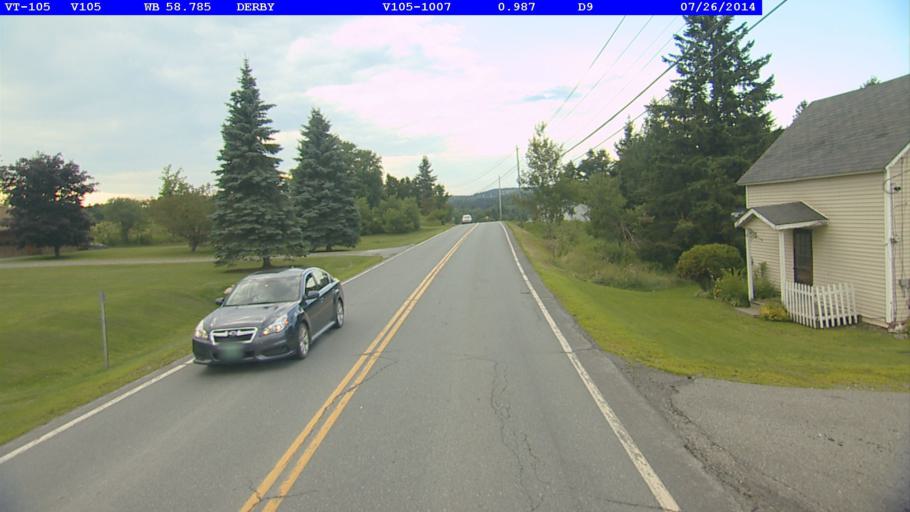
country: US
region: Vermont
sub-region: Orleans County
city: Newport
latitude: 44.9415
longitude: -72.1313
